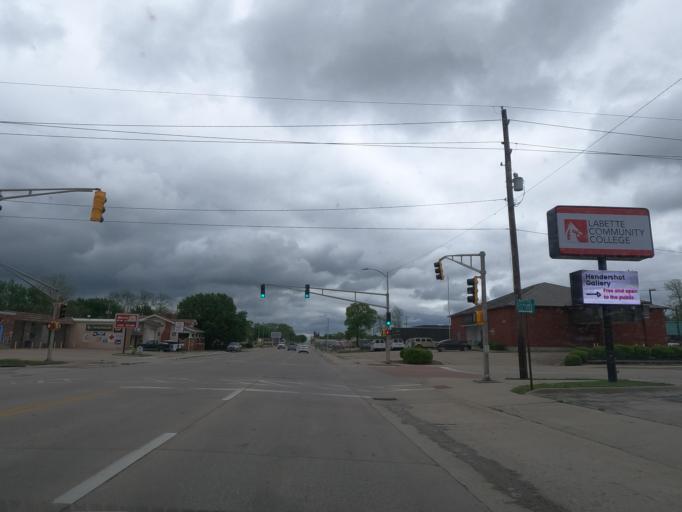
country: US
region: Kansas
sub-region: Labette County
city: Parsons
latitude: 37.3405
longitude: -95.2546
